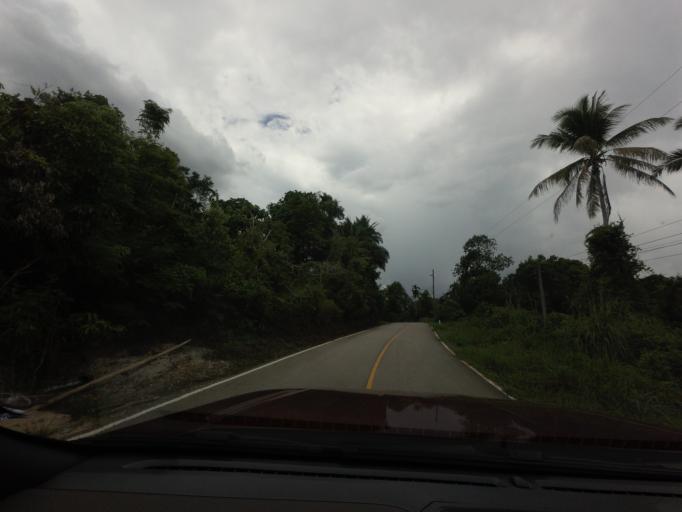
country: TH
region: Narathiwat
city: Sukhirin
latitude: 5.9838
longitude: 101.7059
